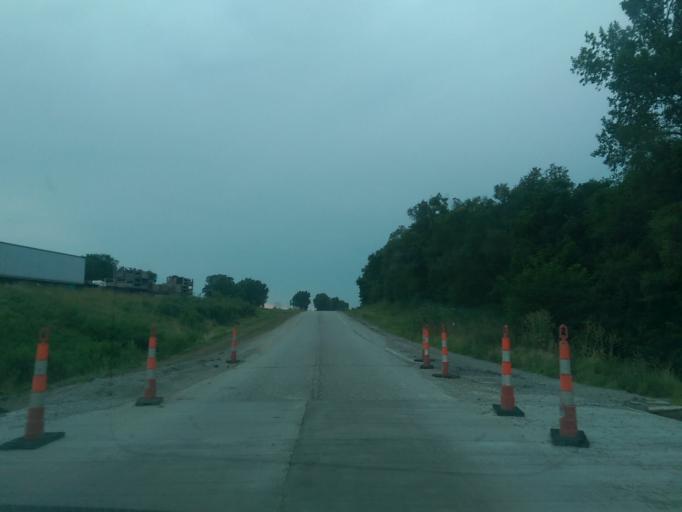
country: US
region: Missouri
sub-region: Holt County
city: Oregon
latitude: 40.0456
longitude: -95.1384
